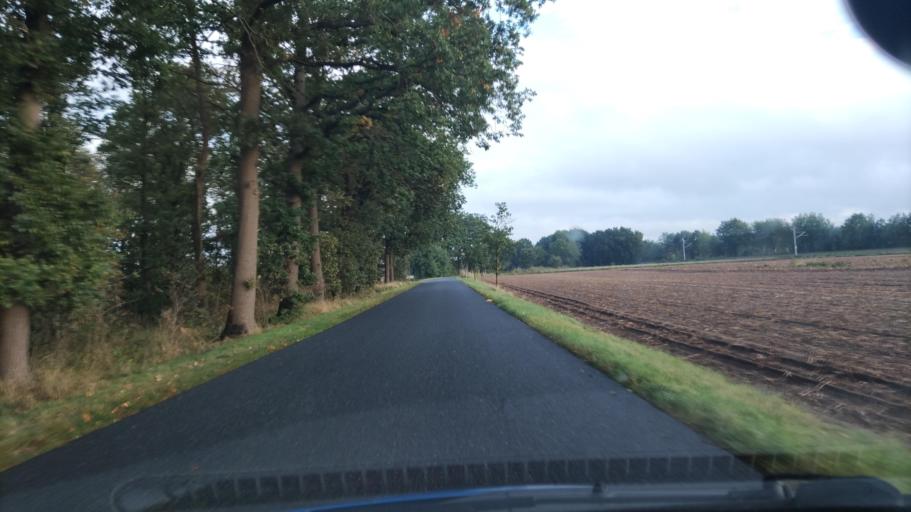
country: DE
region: Lower Saxony
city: Wrestedt
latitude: 52.9042
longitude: 10.6082
